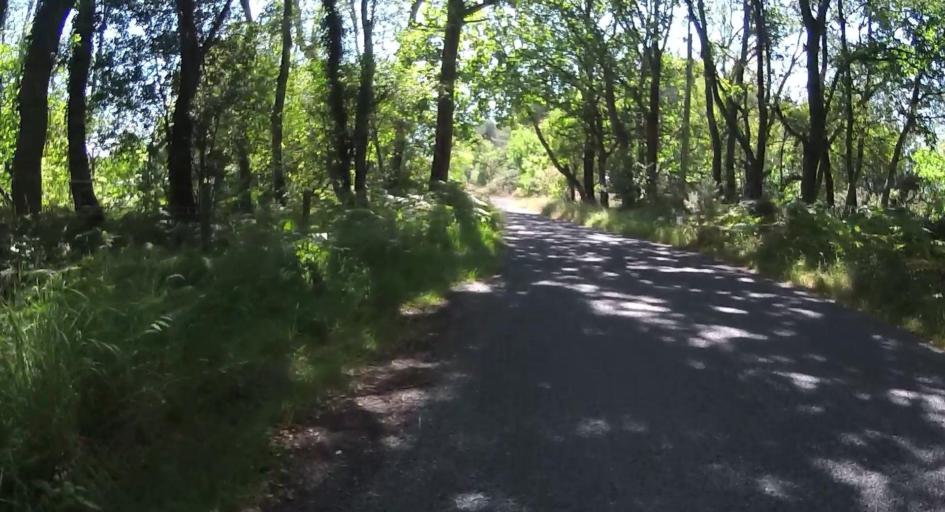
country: GB
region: England
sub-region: Dorset
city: Wareham
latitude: 50.6750
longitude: -2.0617
